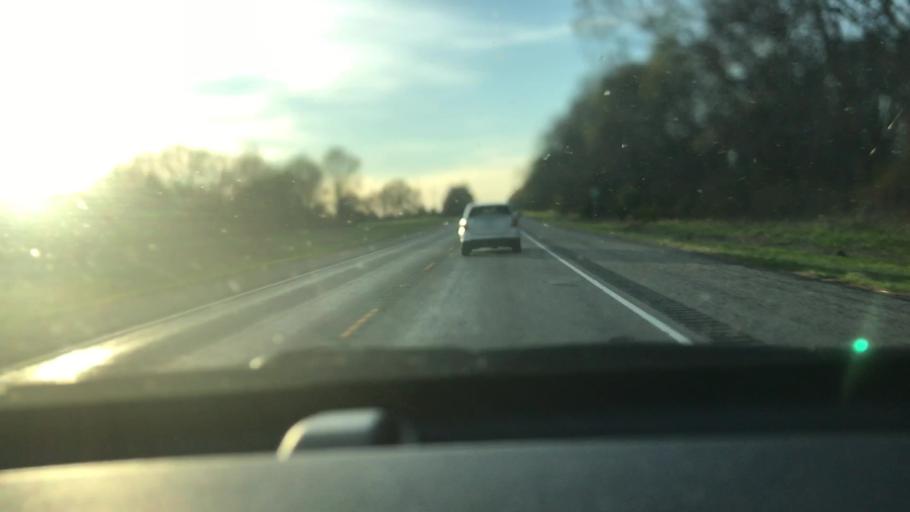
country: US
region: Texas
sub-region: Red River County
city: Clarksville
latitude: 33.5951
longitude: -94.9612
